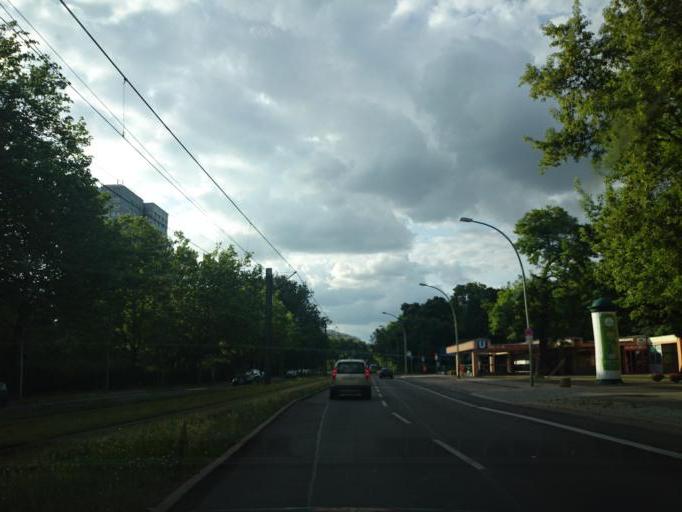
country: DE
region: Berlin
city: Karlshorst
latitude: 52.4978
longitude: 13.5235
